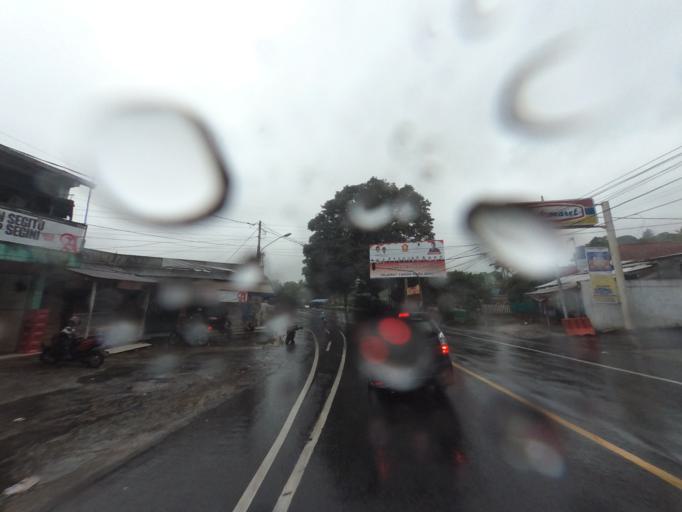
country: ID
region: West Java
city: Caringin
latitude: -6.6534
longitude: 106.8674
